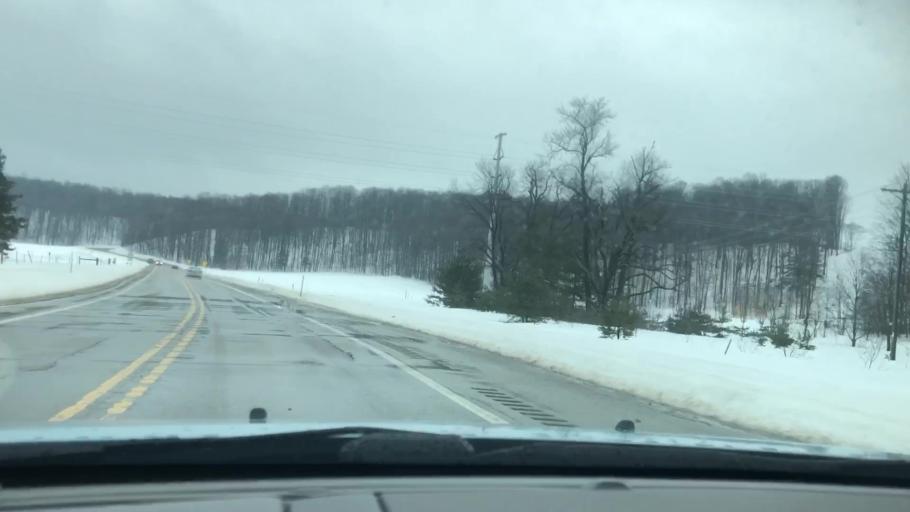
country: US
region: Michigan
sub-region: Charlevoix County
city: Boyne City
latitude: 45.0812
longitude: -84.9197
